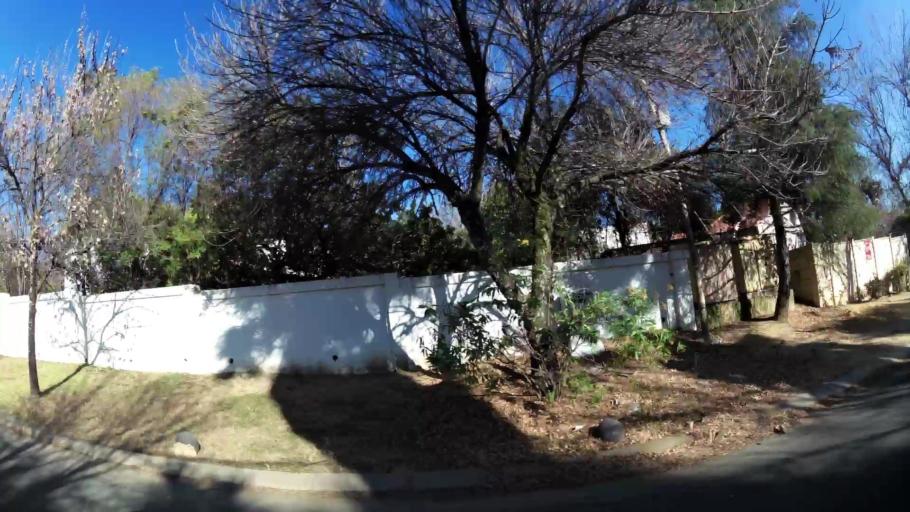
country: ZA
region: Gauteng
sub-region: City of Johannesburg Metropolitan Municipality
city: Diepsloot
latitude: -26.0340
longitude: 27.9798
